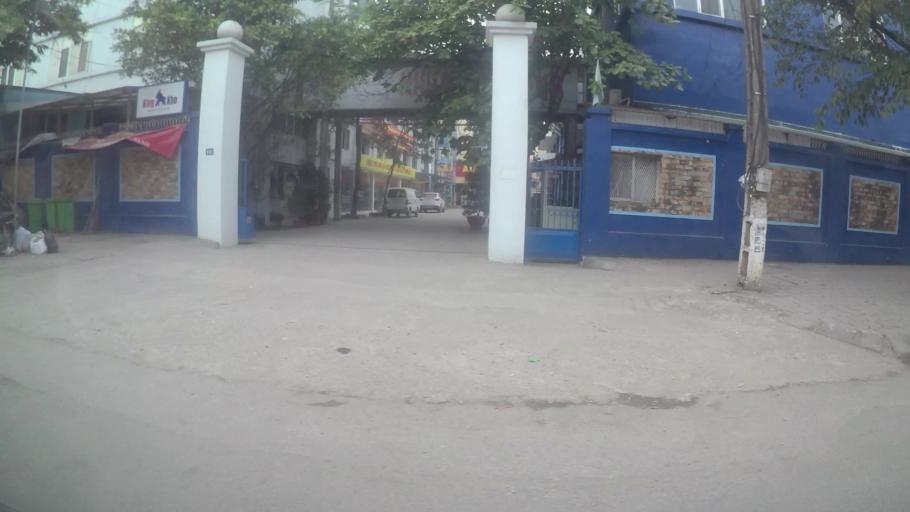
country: VN
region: Ha Noi
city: Ha Dong
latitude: 20.9803
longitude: 105.7719
